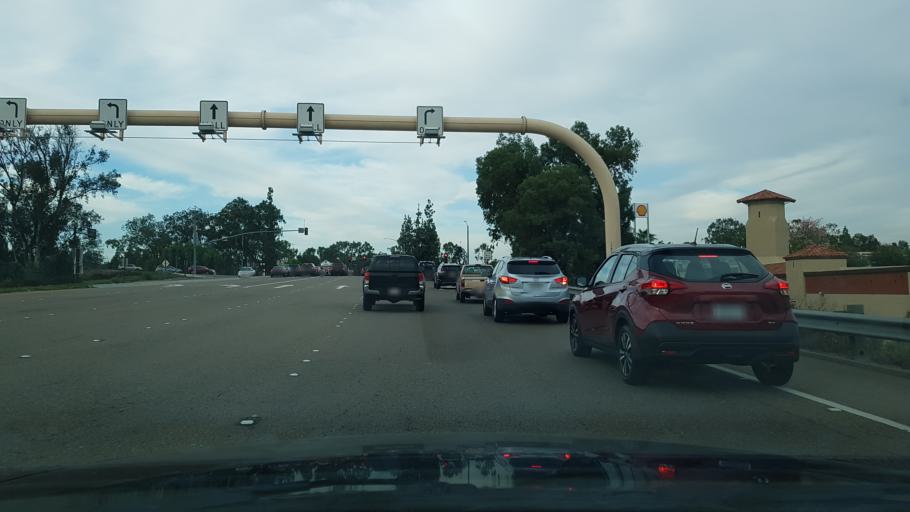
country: US
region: California
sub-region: San Diego County
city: Escondido
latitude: 33.0674
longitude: -117.0682
